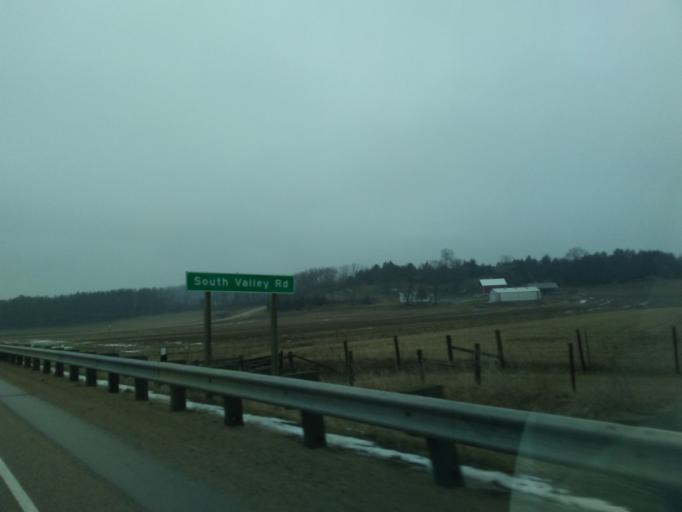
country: US
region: Wisconsin
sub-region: Dane County
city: Black Earth
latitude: 43.1259
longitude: -89.7073
